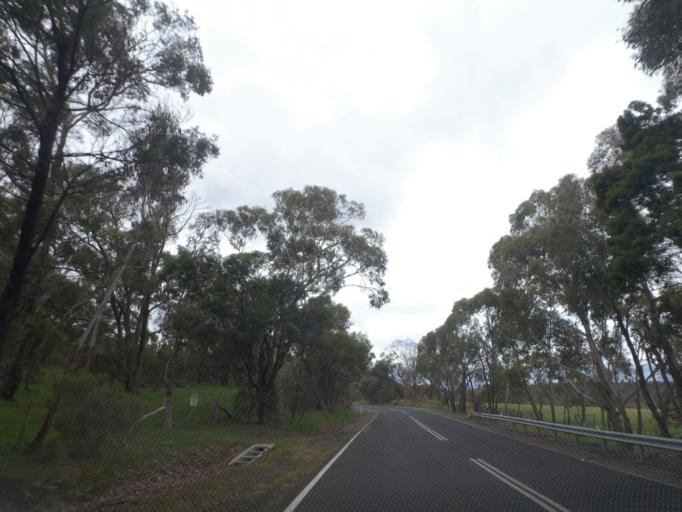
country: AU
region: Victoria
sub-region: Whittlesea
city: Whittlesea
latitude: -37.4927
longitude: 145.0502
